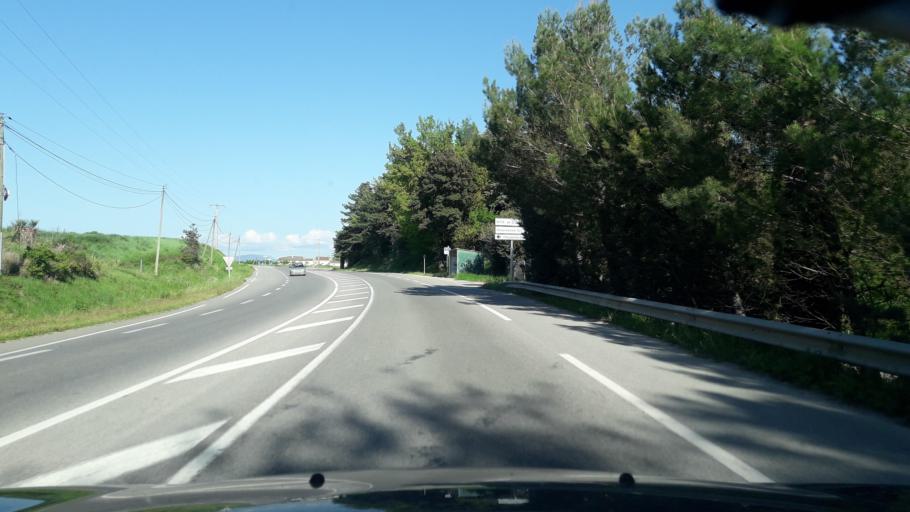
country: FR
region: Rhone-Alpes
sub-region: Departement de la Drome
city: Eurre
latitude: 44.7226
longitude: 4.9818
